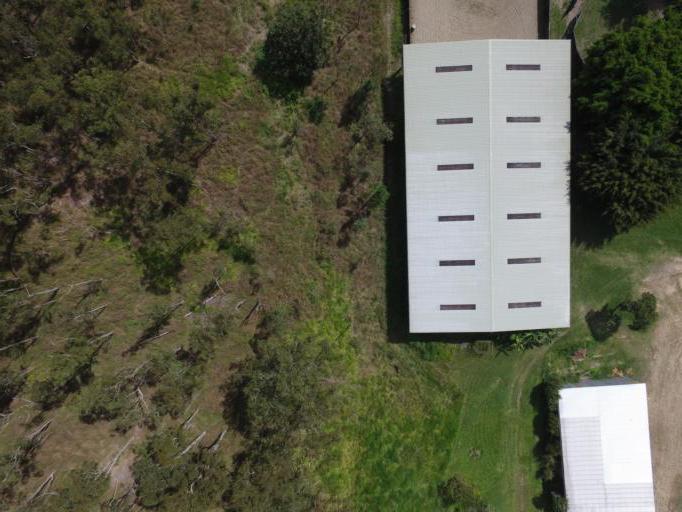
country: AU
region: Queensland
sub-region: Tablelands
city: Atherton
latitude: -17.3033
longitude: 145.4565
